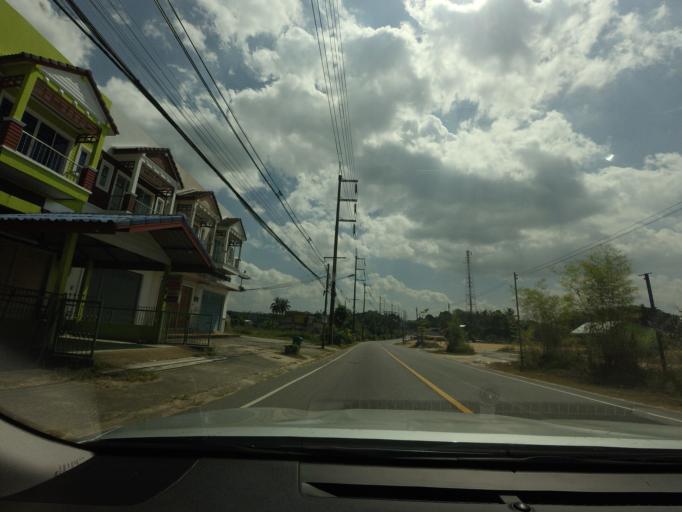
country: TH
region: Phangnga
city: Thai Mueang
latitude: 8.3927
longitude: 98.2657
